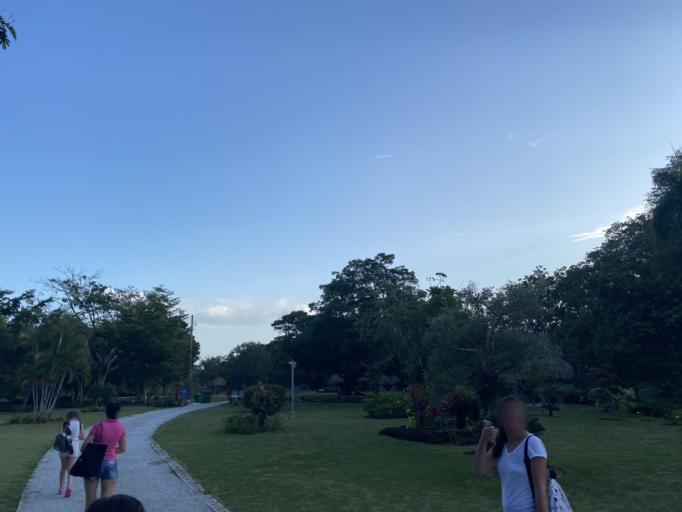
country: DO
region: Maria Trinidad Sanchez
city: La Entrada
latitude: 19.5644
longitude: -69.9079
